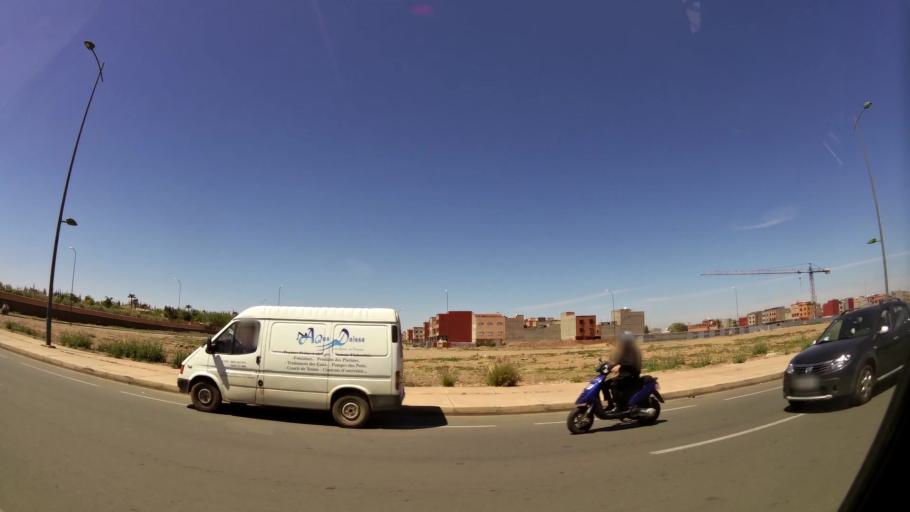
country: MA
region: Marrakech-Tensift-Al Haouz
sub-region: Marrakech
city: Marrakesh
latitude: 31.5516
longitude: -7.9744
